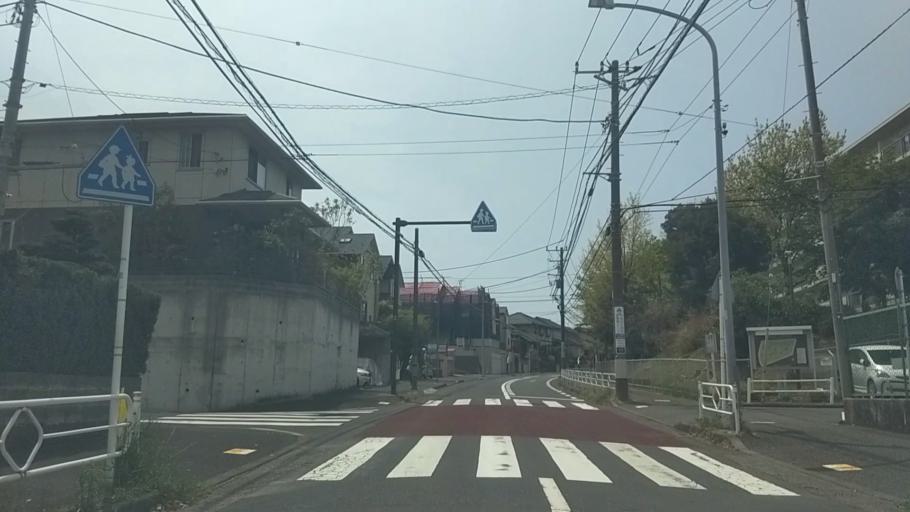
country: JP
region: Kanagawa
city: Kamakura
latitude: 35.3698
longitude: 139.5870
